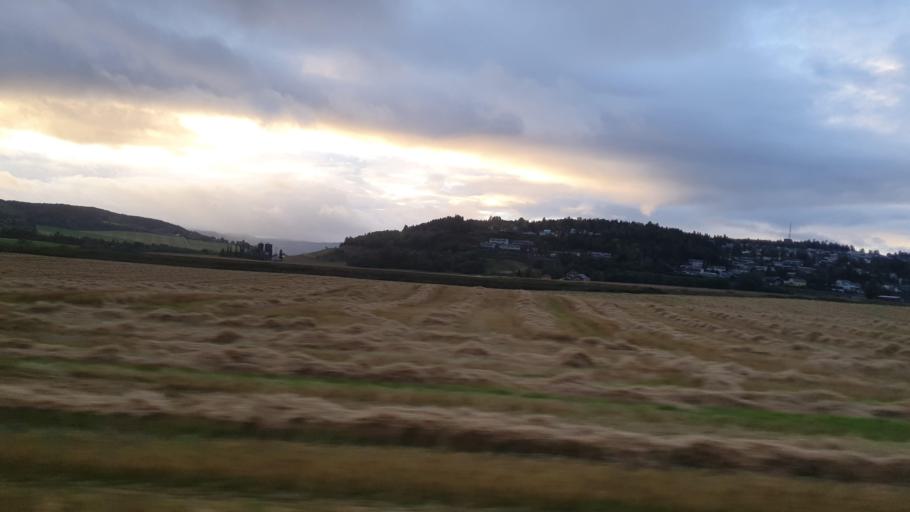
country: NO
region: Nord-Trondelag
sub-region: Levanger
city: Skogn
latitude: 63.6913
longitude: 11.1898
